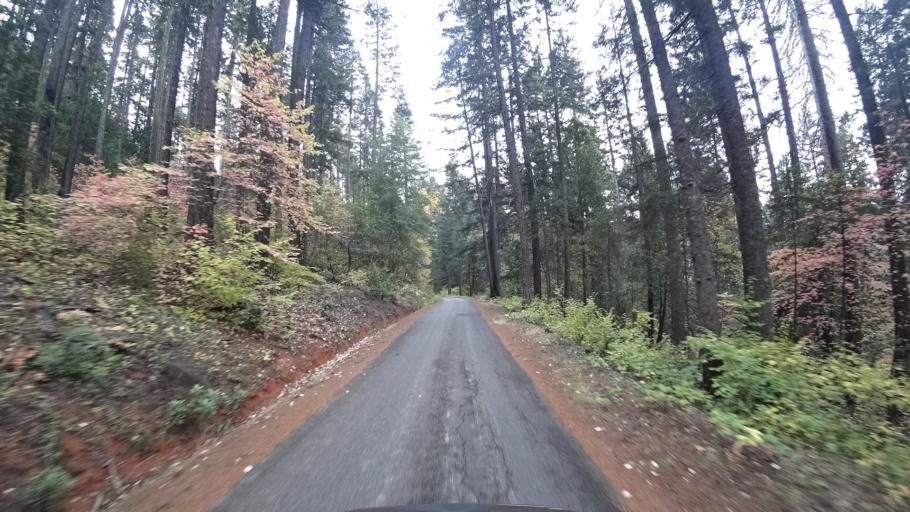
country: US
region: California
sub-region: Siskiyou County
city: Happy Camp
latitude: 41.8062
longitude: -123.3392
